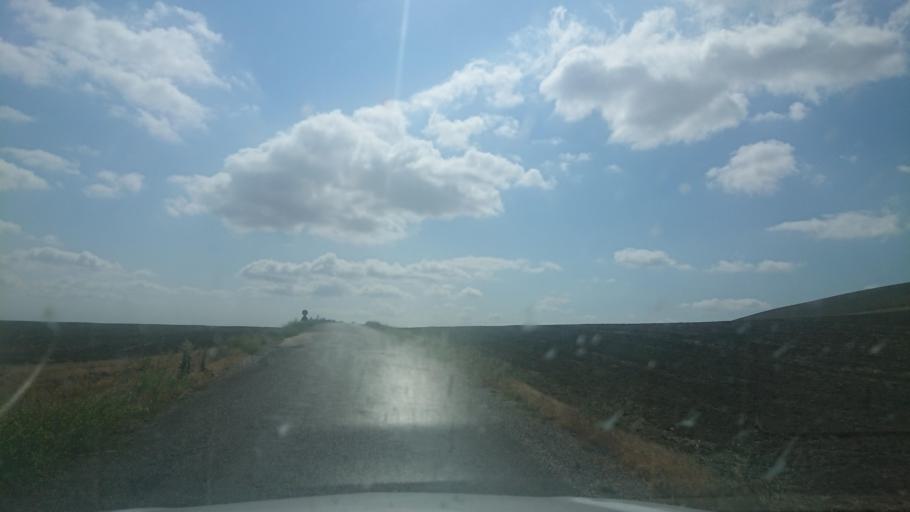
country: TR
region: Aksaray
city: Sariyahsi
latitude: 39.0030
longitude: 33.9677
